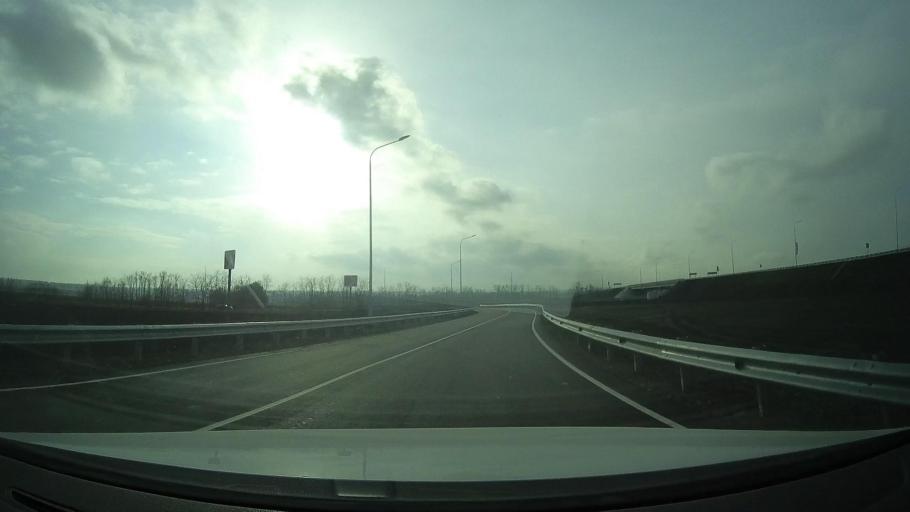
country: RU
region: Rostov
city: Grushevskaya
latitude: 47.4562
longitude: 39.8859
